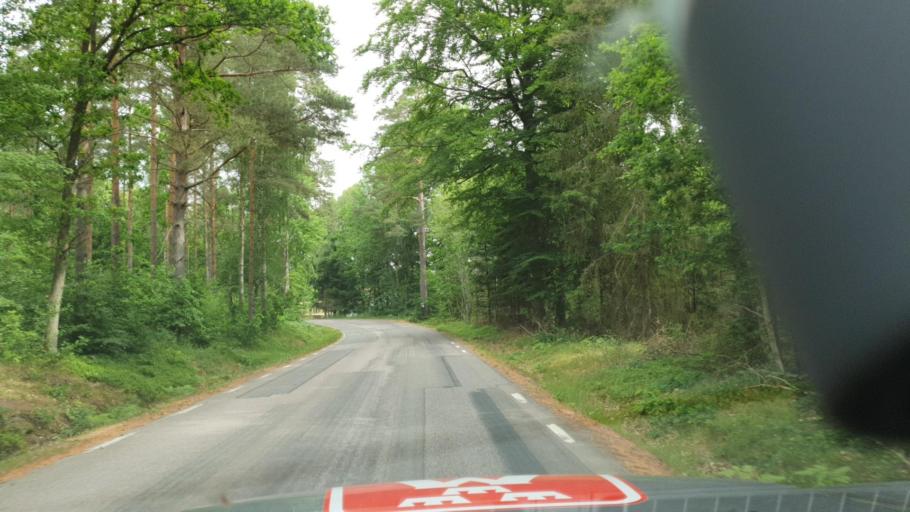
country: SE
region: Kalmar
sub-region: Torsas Kommun
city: Torsas
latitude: 56.4934
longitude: 16.1028
